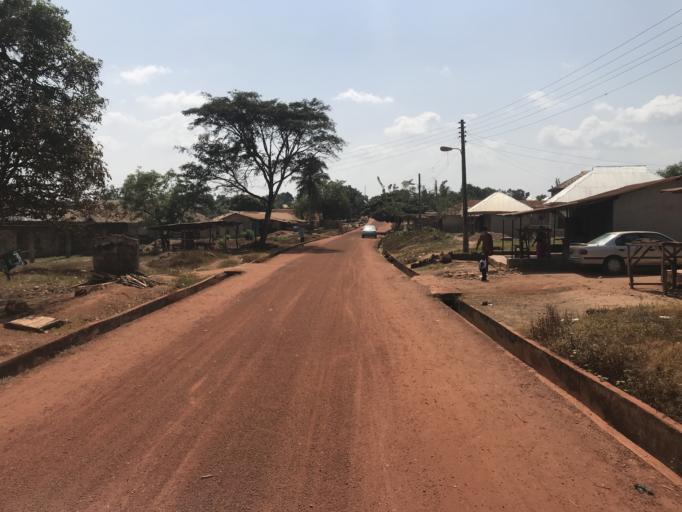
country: NG
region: Osun
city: Ifon
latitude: 7.8686
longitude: 4.4785
